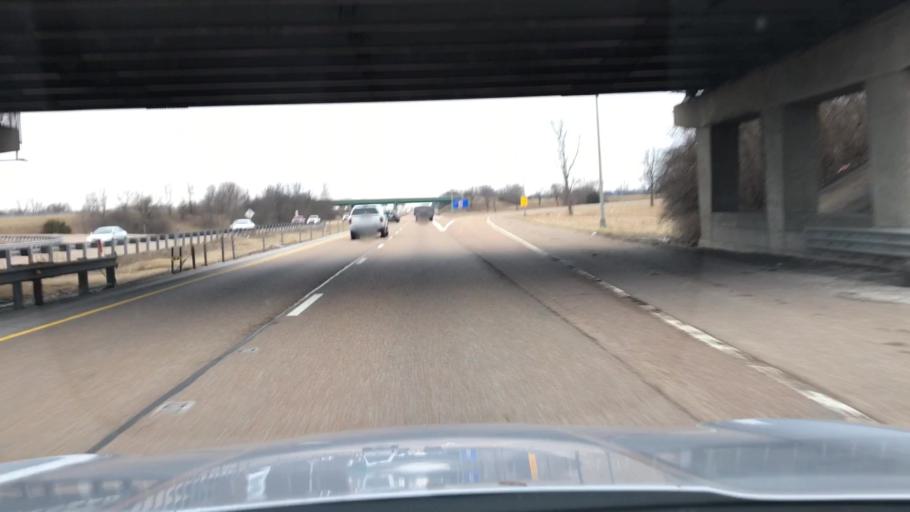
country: US
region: Illinois
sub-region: Madison County
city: Troy
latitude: 38.7521
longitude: -89.9073
